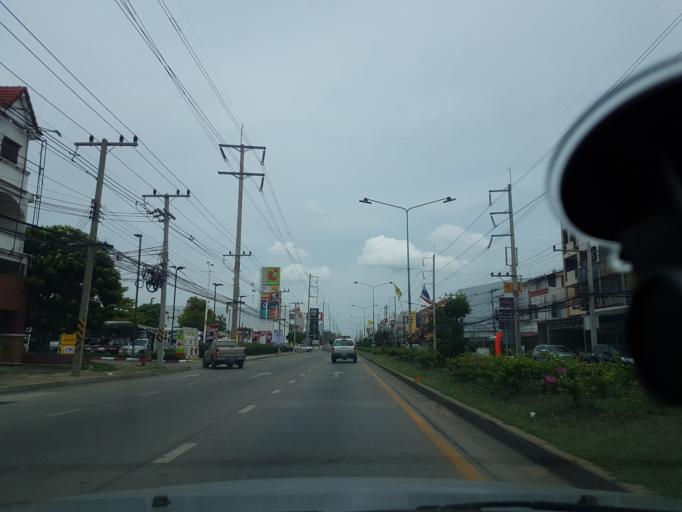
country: TH
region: Lop Buri
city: Lop Buri
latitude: 14.7985
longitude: 100.6622
